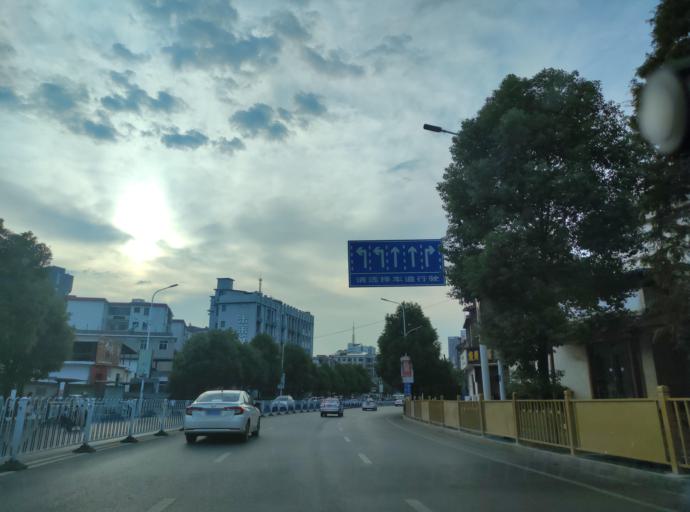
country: CN
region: Jiangxi Sheng
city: Pingxiang
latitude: 27.6338
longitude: 113.8589
